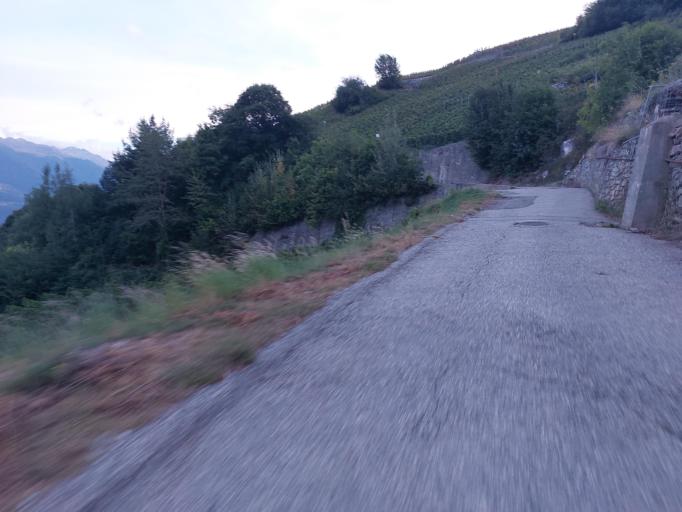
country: CH
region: Valais
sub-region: Conthey District
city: Conthey
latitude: 46.2484
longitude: 7.3075
